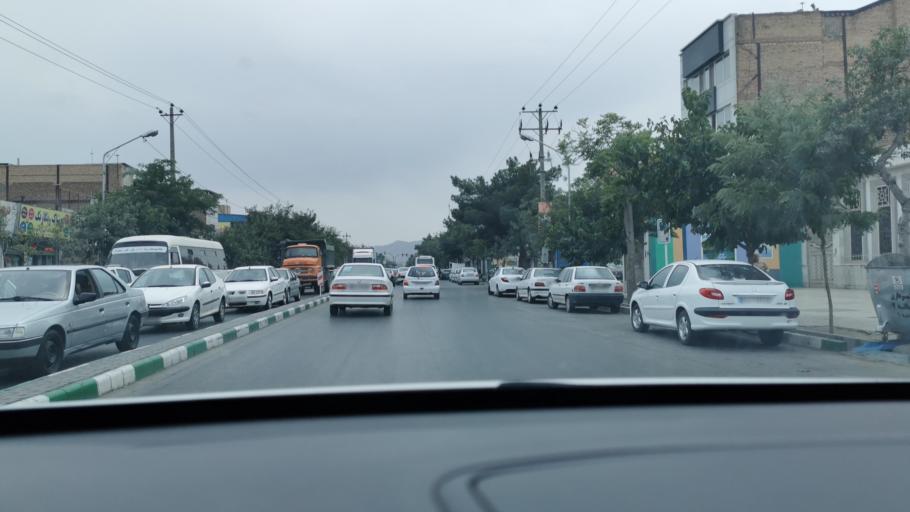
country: IR
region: Razavi Khorasan
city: Mashhad
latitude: 36.3194
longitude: 59.6192
